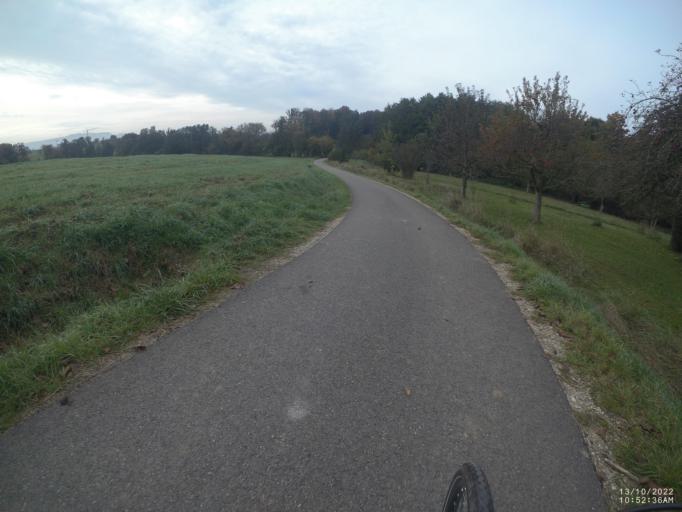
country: DE
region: Baden-Wuerttemberg
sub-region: Regierungsbezirk Stuttgart
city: Albershausen
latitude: 48.6946
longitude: 9.5501
